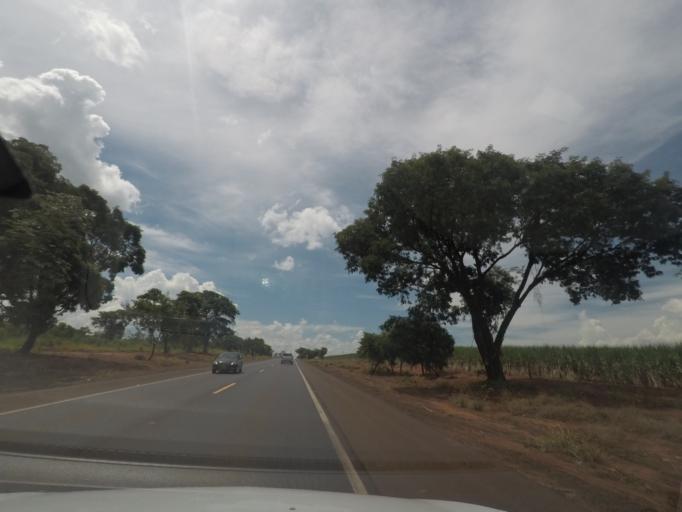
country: BR
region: Sao Paulo
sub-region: Barretos
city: Barretos
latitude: -20.2845
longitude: -48.6705
